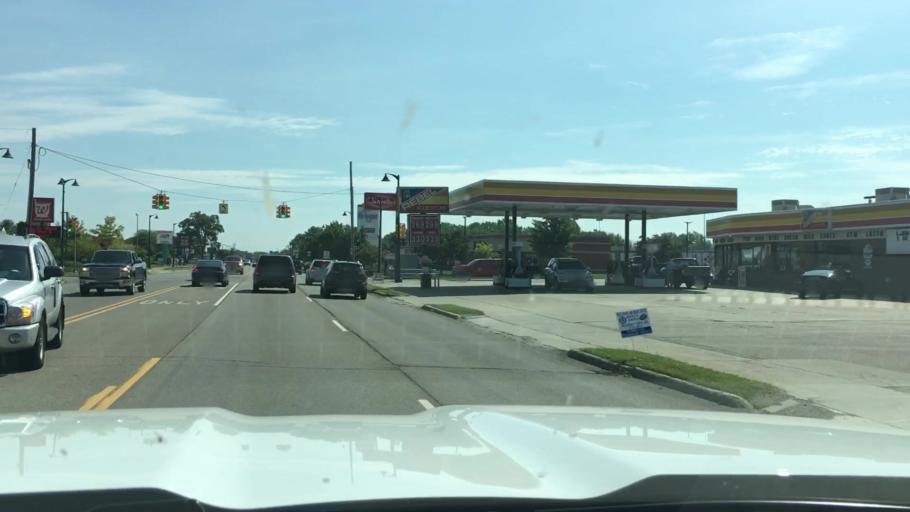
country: US
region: Michigan
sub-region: Bay County
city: Essexville
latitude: 43.5949
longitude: -83.8481
